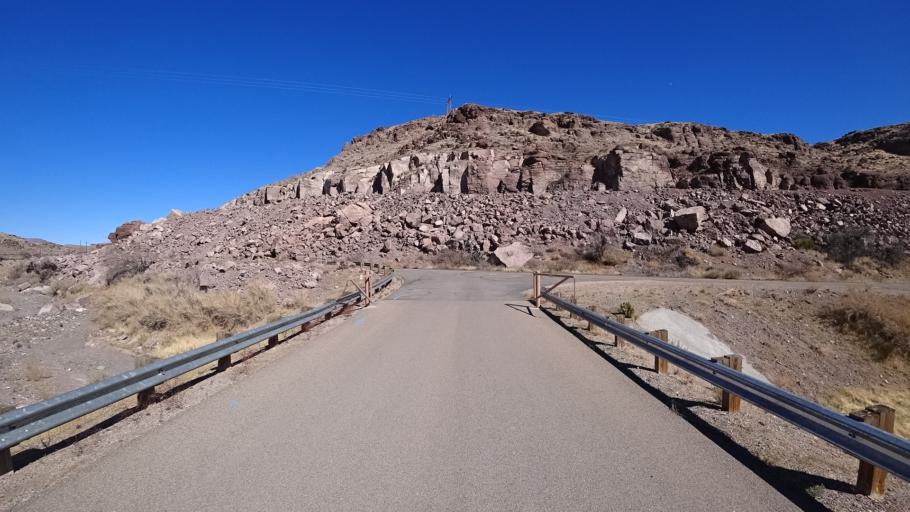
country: US
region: Arizona
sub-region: Mohave County
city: Kingman
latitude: 35.1775
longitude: -114.0629
